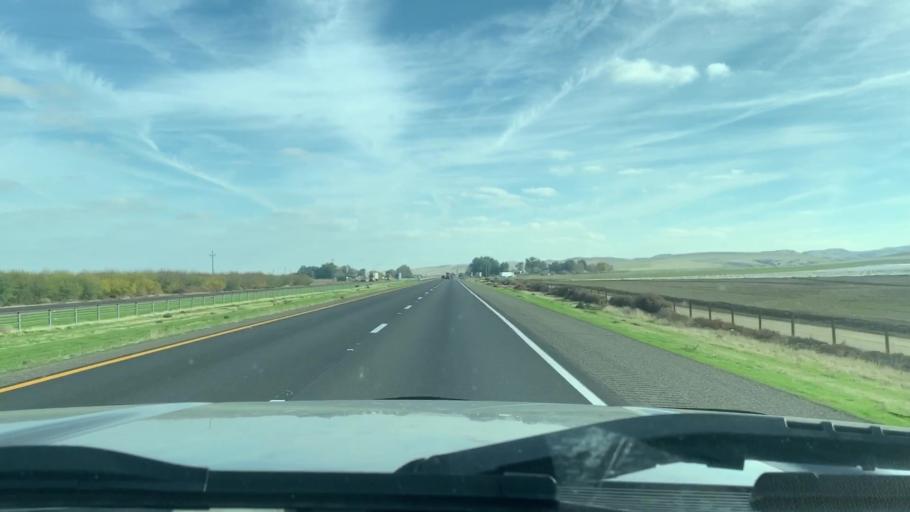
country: US
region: California
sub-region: Kings County
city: Avenal
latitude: 36.0961
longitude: -120.1211
